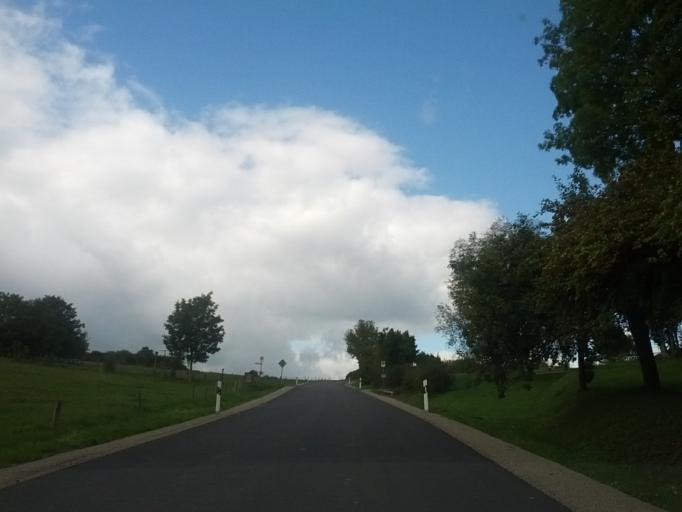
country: DE
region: Hesse
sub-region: Regierungsbezirk Kassel
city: Weissenborn
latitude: 51.0707
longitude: 10.0703
